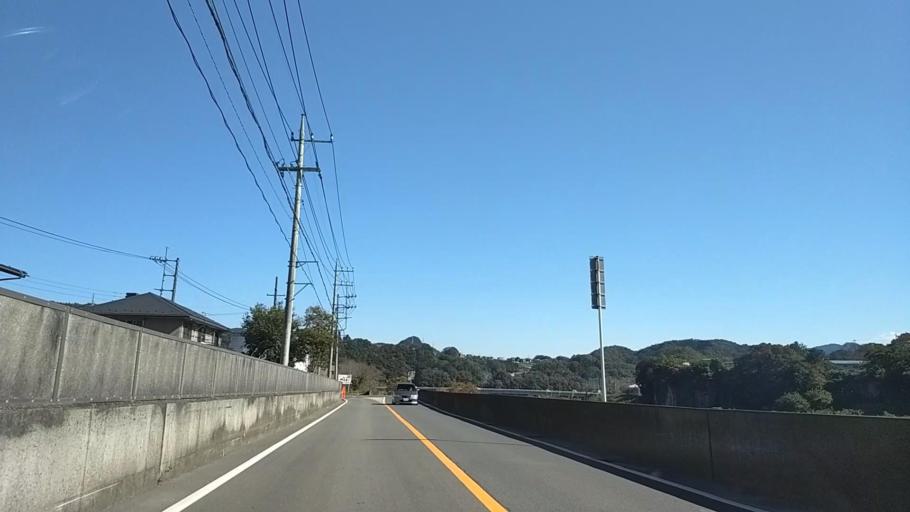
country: JP
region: Yamanashi
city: Uenohara
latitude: 35.6166
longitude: 139.1134
